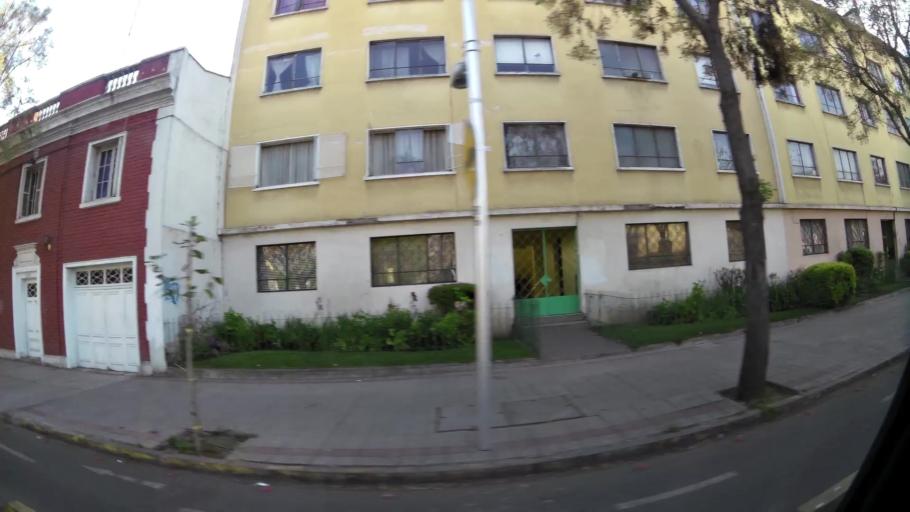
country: CL
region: Santiago Metropolitan
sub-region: Provincia de Santiago
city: Santiago
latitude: -33.4422
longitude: -70.6700
